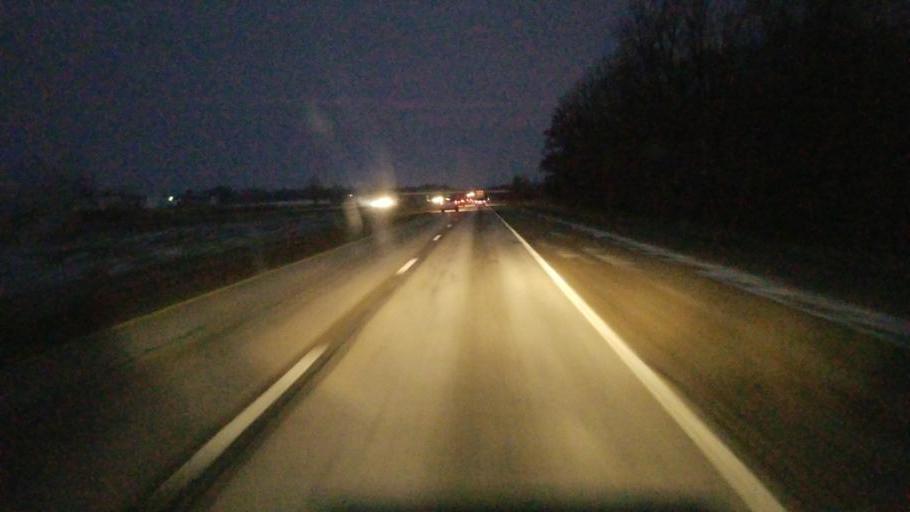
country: US
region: Ohio
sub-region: Preble County
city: Eaton
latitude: 39.8357
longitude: -84.6699
